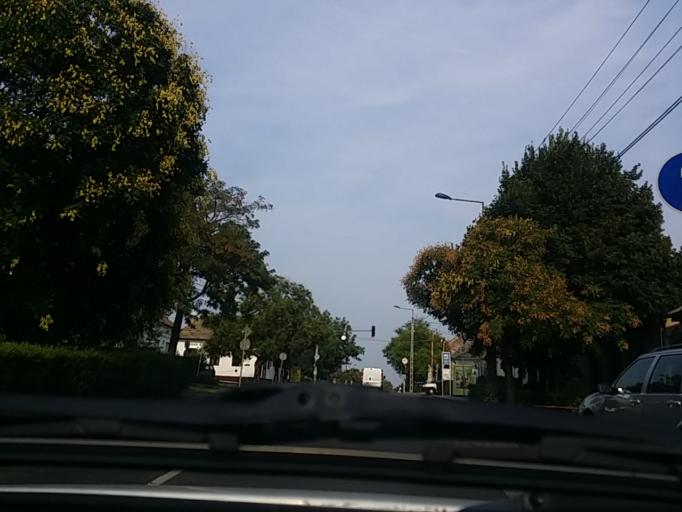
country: HU
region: Pest
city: Budaors
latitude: 47.4615
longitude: 18.9680
